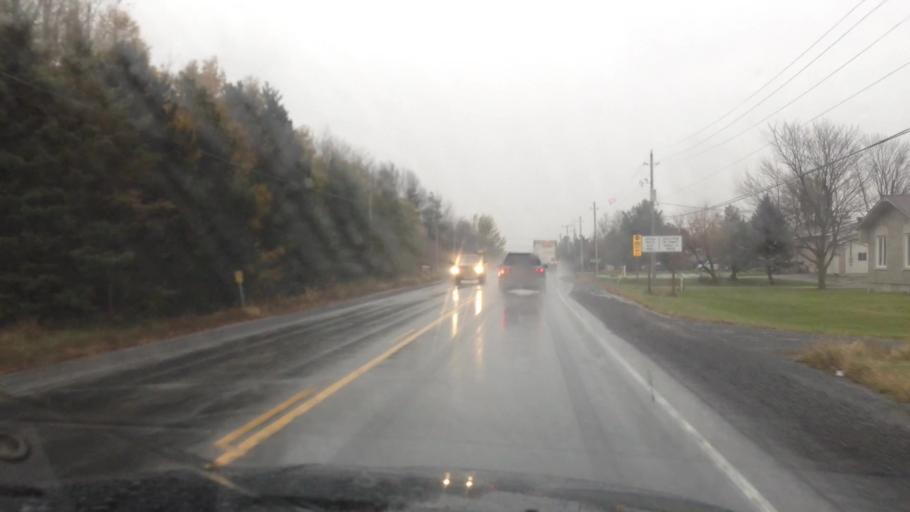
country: CA
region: Ontario
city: Bourget
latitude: 45.2760
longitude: -75.3143
